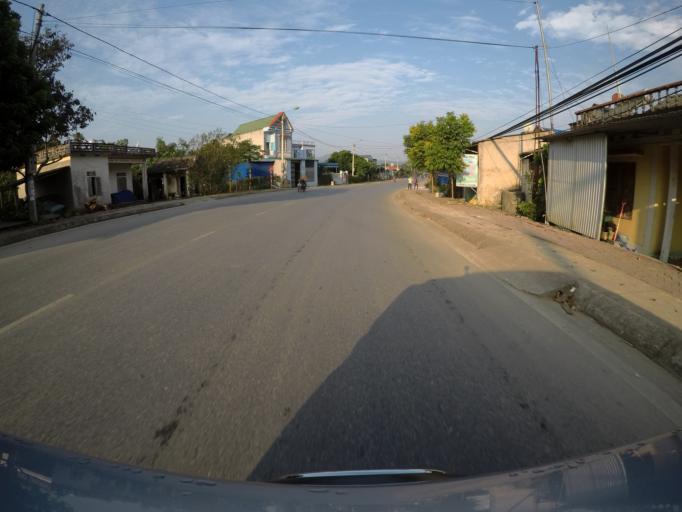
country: VN
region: Lai Chau
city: Tam Duong
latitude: 22.3177
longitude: 103.6420
